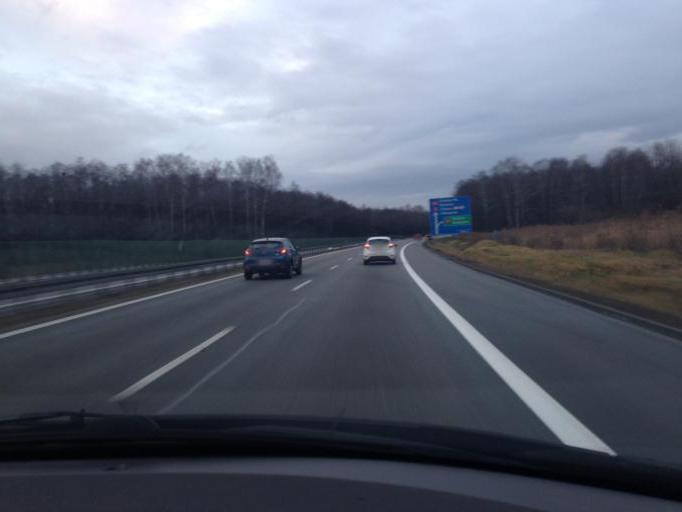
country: PL
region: Lesser Poland Voivodeship
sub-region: Krakow
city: Sidzina
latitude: 50.0148
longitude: 19.8442
